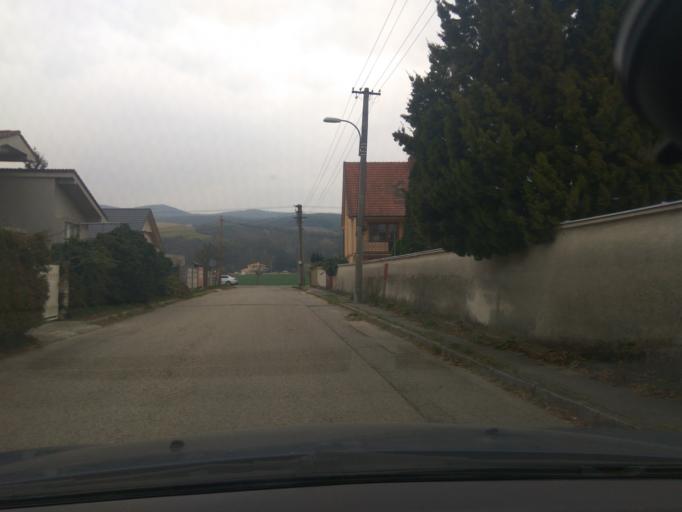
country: SK
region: Trnavsky
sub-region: Okres Trnava
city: Piestany
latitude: 48.5944
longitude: 17.8584
